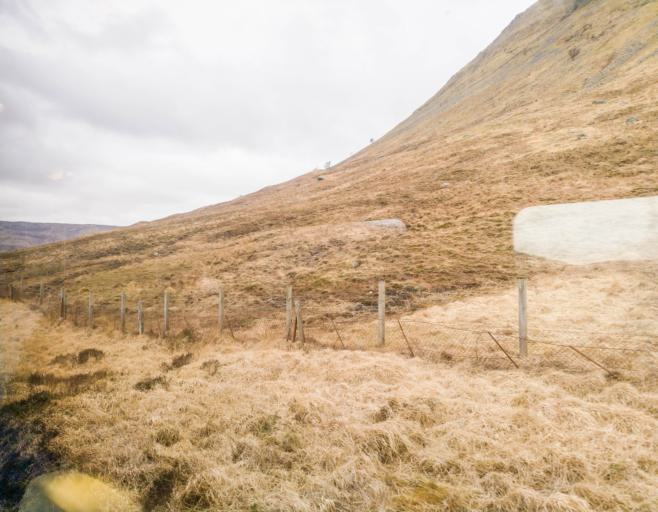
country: GB
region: Scotland
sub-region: Argyll and Bute
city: Garelochhead
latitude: 56.4874
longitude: -4.7189
